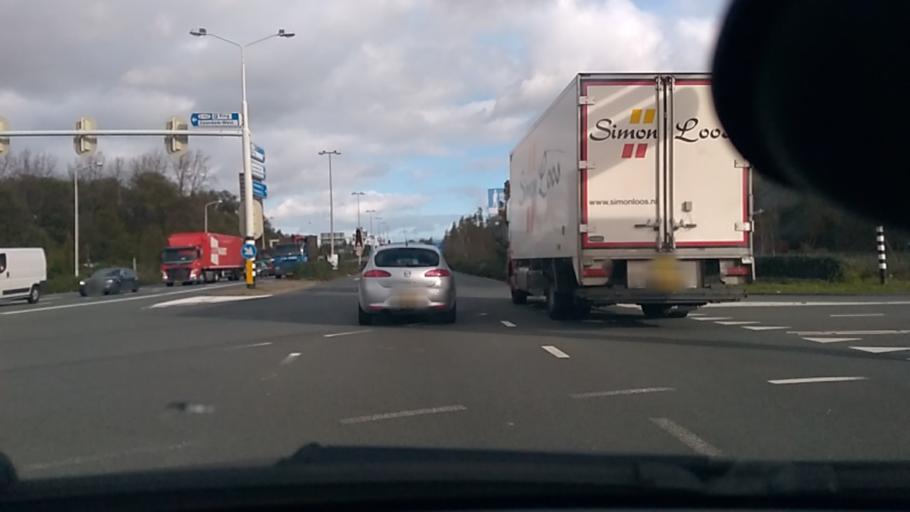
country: NL
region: North Holland
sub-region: Gemeente Zaanstad
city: Zaandam
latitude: 52.4265
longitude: 4.8274
